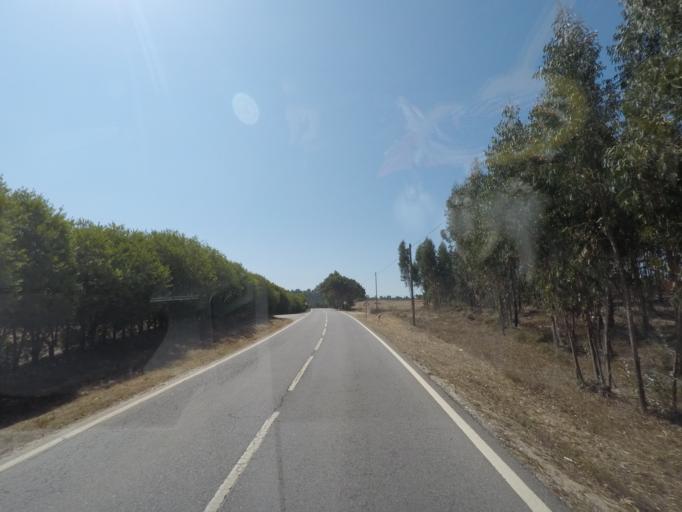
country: PT
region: Beja
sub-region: Odemira
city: Sao Teotonio
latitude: 37.5374
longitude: -8.6913
